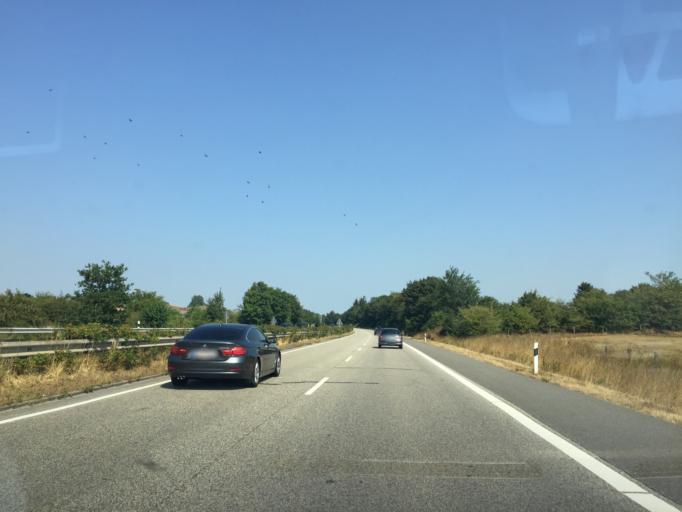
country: DE
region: Schleswig-Holstein
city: Handewitt
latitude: 54.7730
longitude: 9.3501
